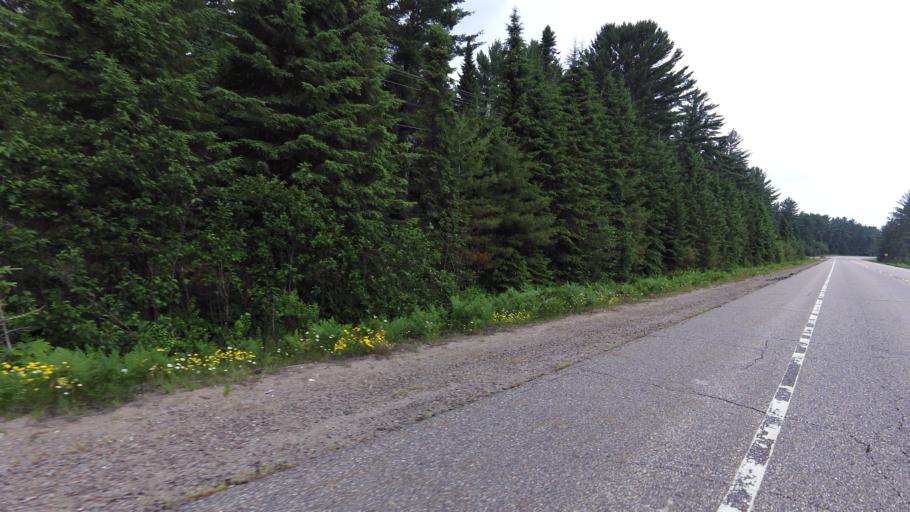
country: CA
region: Ontario
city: Huntsville
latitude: 45.5756
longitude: -78.5238
